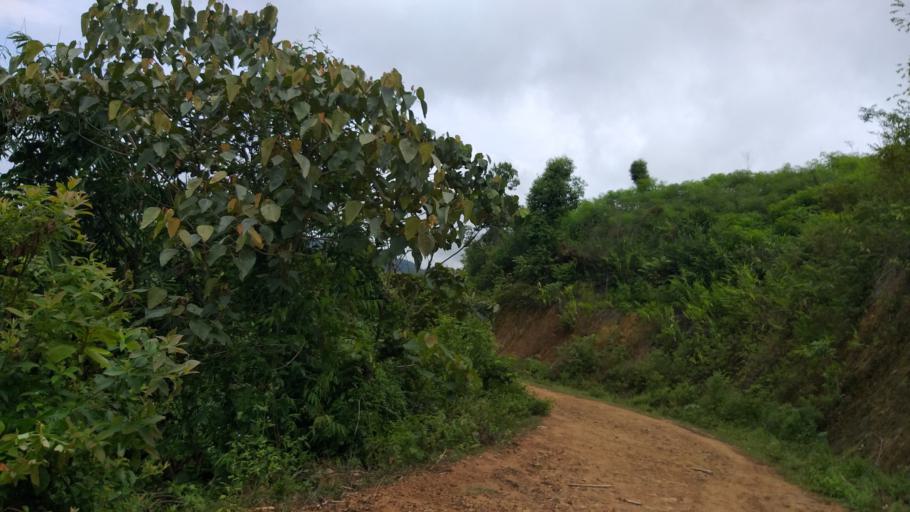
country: LA
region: Phongsali
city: Khoa
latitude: 21.3943
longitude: 102.6667
